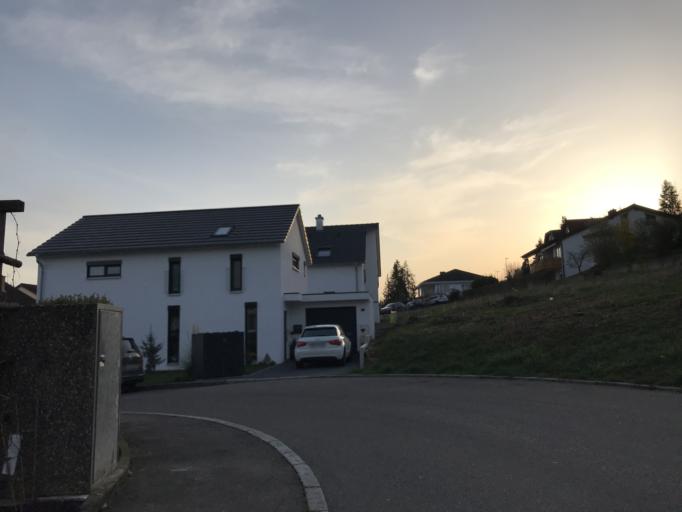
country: DE
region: Baden-Wuerttemberg
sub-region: Regierungsbezirk Stuttgart
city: Unterensingen
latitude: 48.6547
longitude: 9.3502
